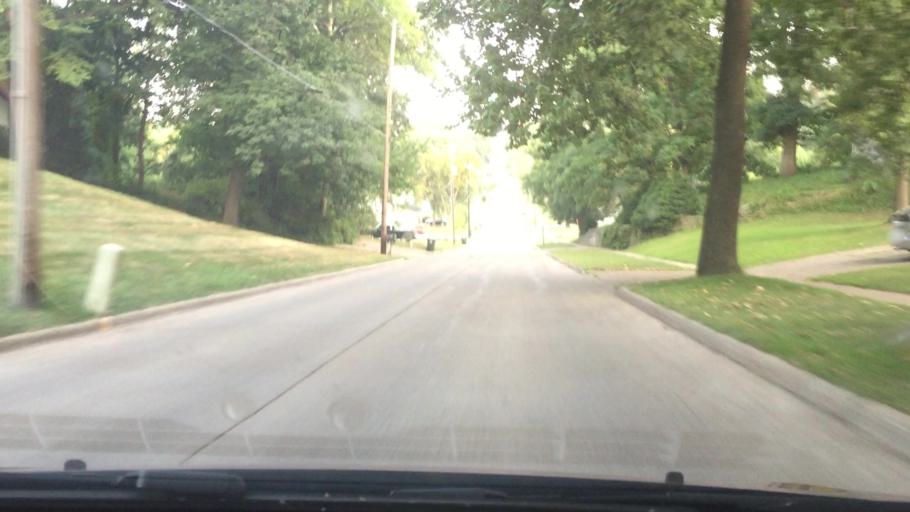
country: US
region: Iowa
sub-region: Muscatine County
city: Muscatine
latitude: 41.4288
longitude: -91.0592
